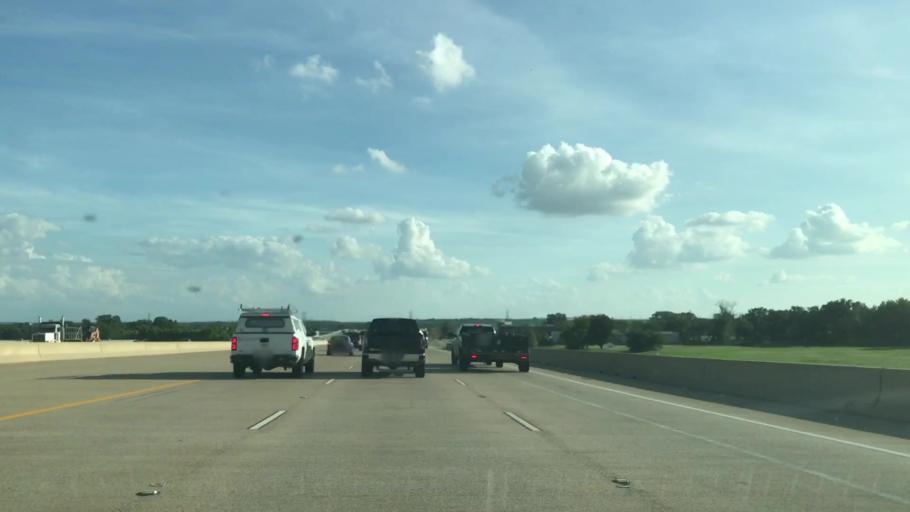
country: US
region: Texas
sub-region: Dallas County
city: Grand Prairie
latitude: 32.7992
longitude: -97.0187
